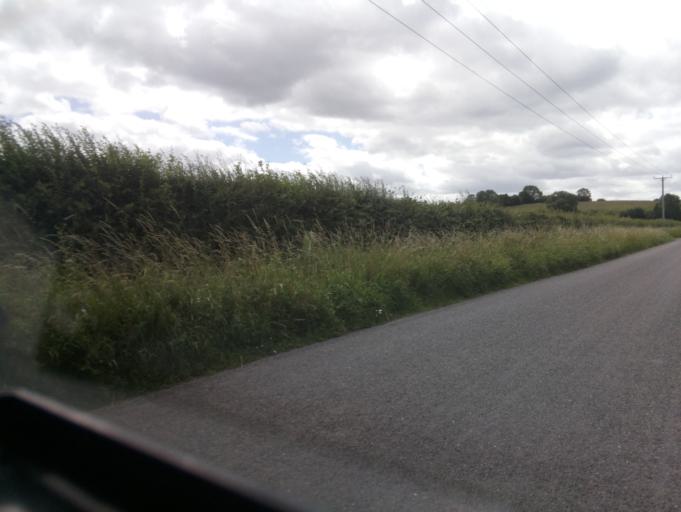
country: GB
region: England
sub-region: Nottinghamshire
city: Ruddington
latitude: 52.8581
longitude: -1.0994
